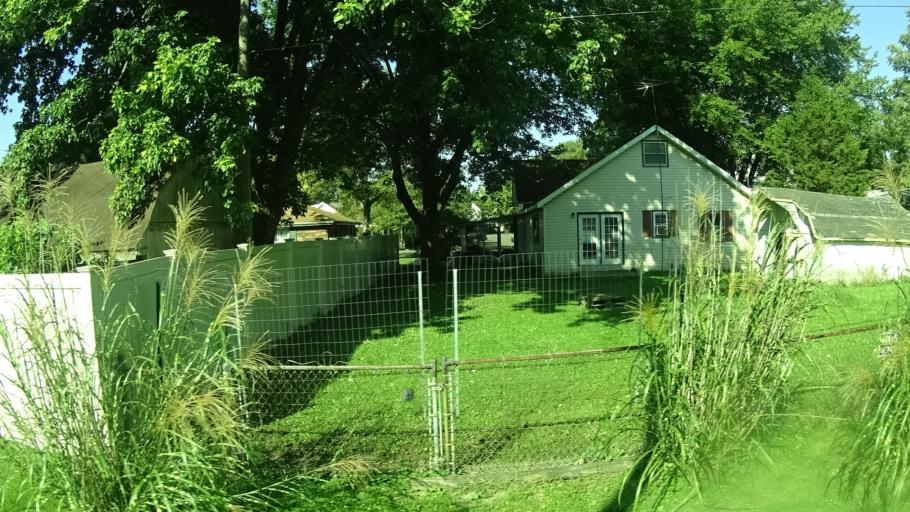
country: US
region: Indiana
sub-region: Madison County
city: Lapel
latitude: 40.0663
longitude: -85.8440
